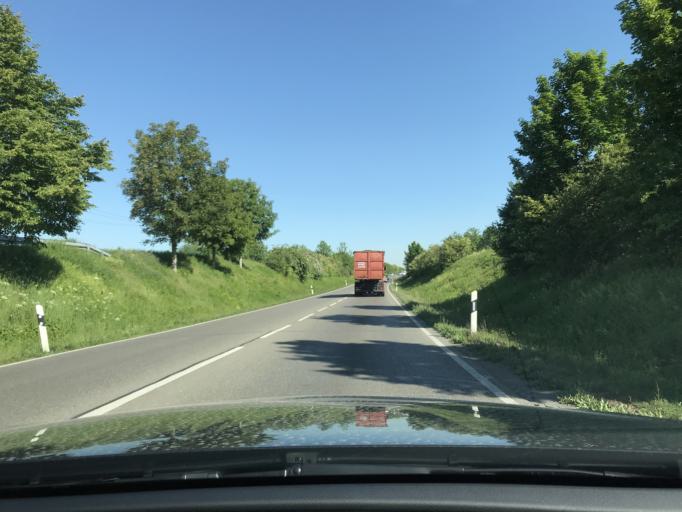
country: DE
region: Baden-Wuerttemberg
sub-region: Regierungsbezirk Stuttgart
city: Fellbach
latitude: 48.8202
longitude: 9.2923
